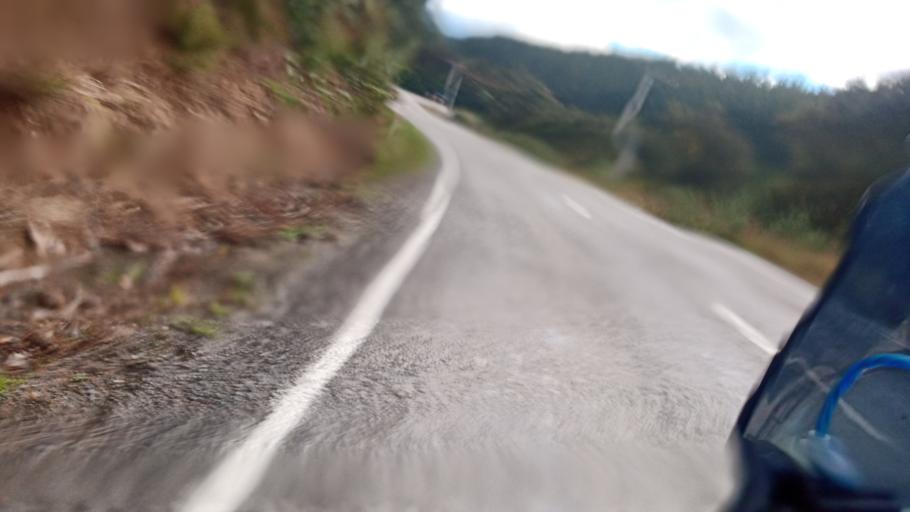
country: NZ
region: Gisborne
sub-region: Gisborne District
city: Gisborne
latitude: -37.9868
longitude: 178.2763
